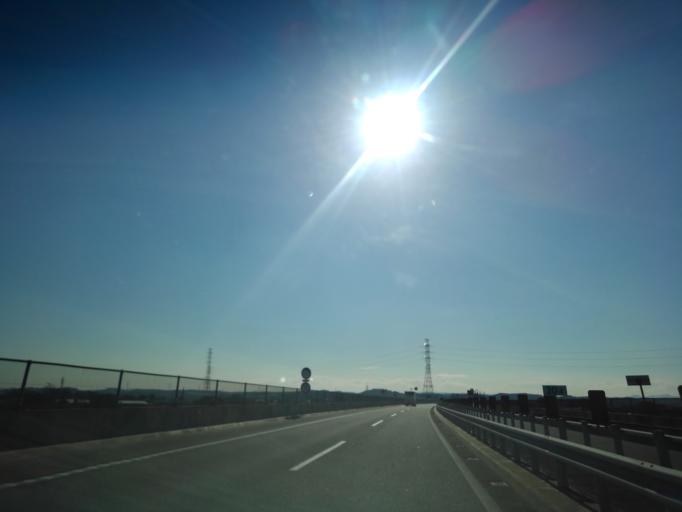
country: JP
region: Chiba
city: Kisarazu
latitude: 35.4037
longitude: 139.9656
